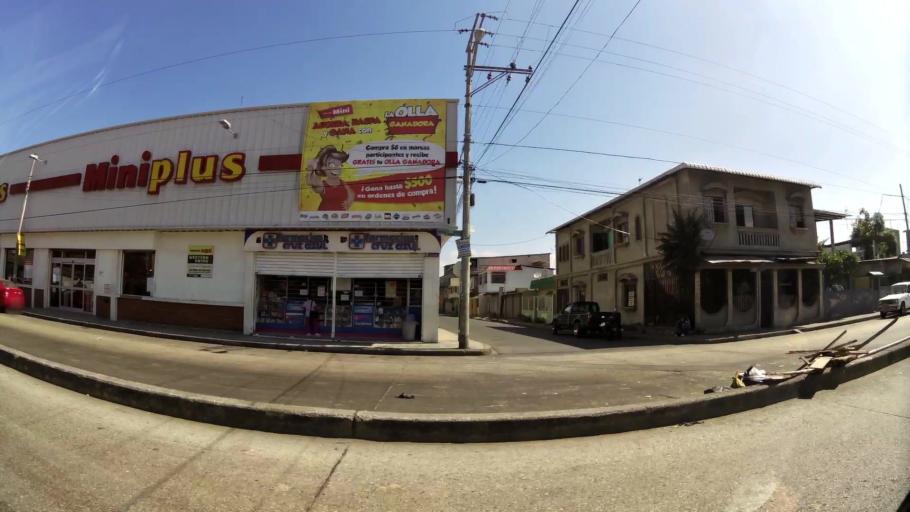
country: EC
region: Guayas
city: Guayaquil
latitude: -2.2320
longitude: -79.9396
